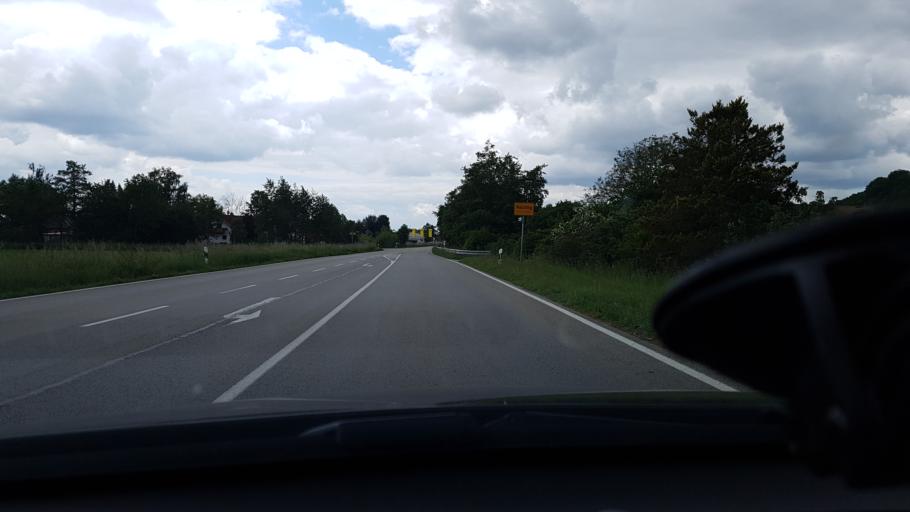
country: DE
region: Bavaria
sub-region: Lower Bavaria
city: Malching
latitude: 48.3185
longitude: 13.1967
